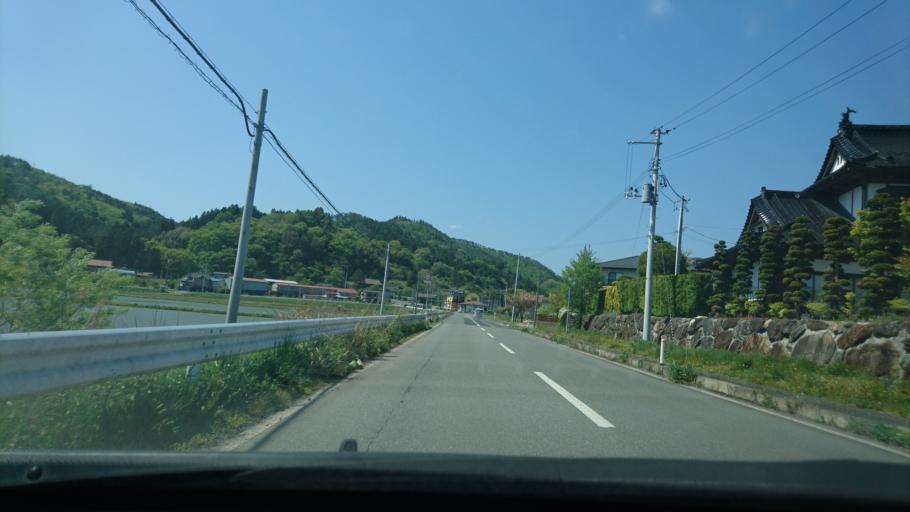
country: JP
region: Iwate
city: Ichinoseki
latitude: 38.9144
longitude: 141.2543
